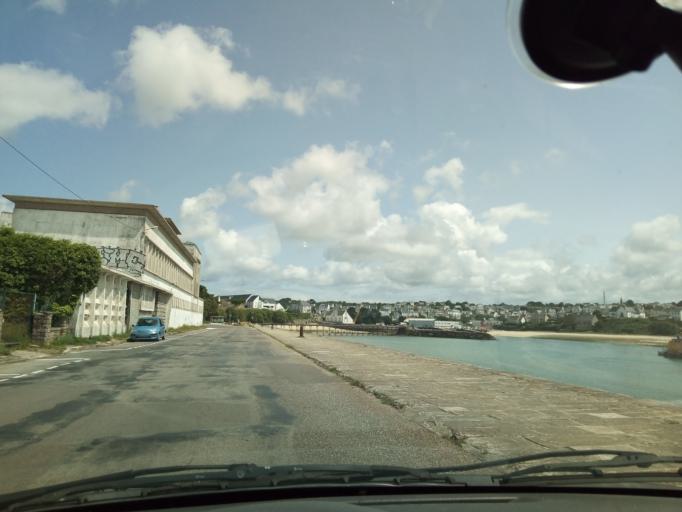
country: FR
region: Brittany
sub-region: Departement du Finistere
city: Audierne
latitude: 48.0149
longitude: -4.5391
